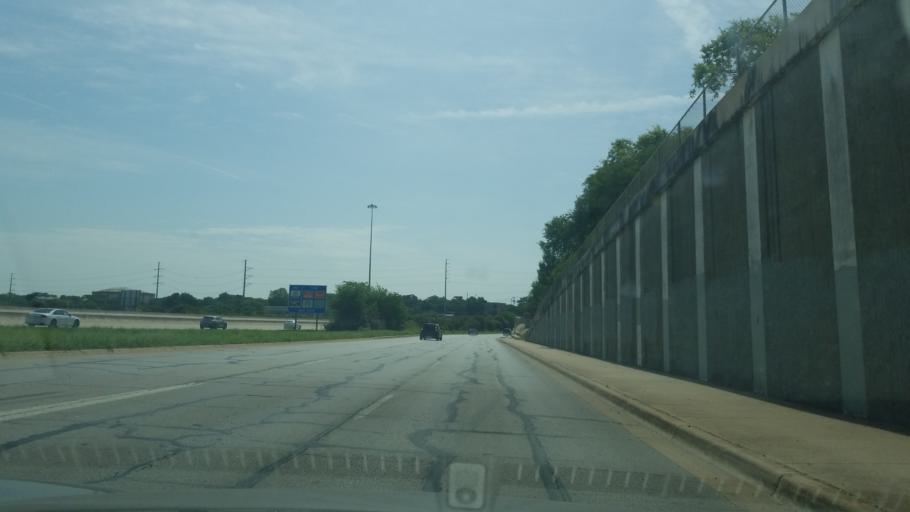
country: US
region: Texas
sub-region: Travis County
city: Austin
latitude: 30.2273
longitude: -97.7746
